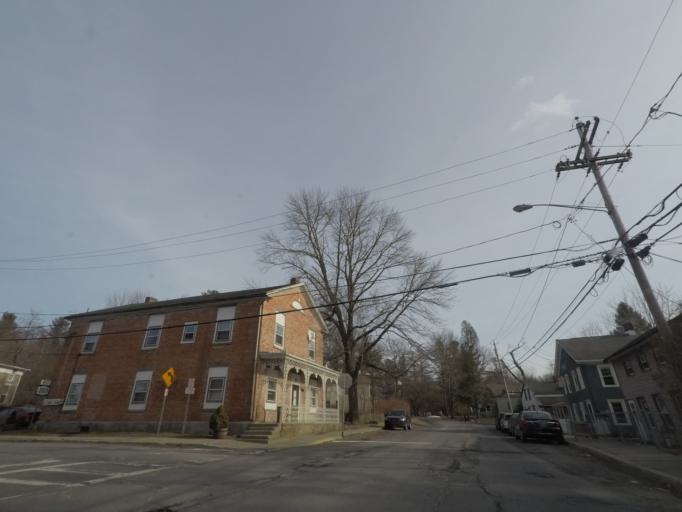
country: US
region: New York
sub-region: Columbia County
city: Valatie
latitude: 42.4129
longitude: -73.6720
